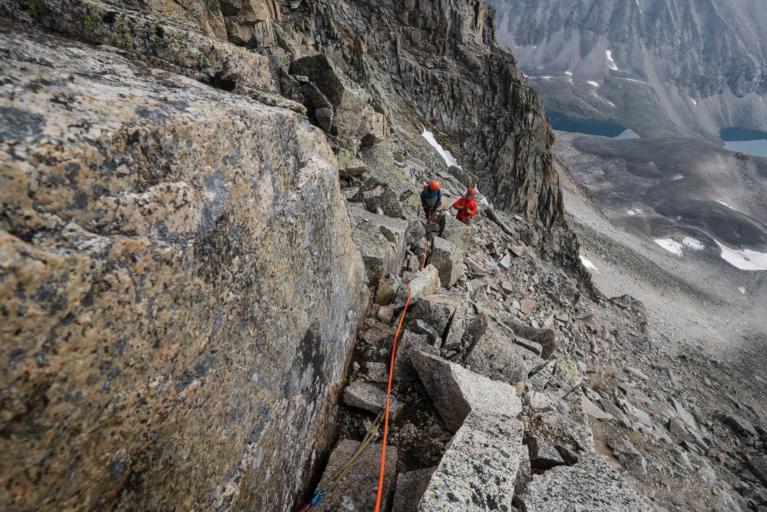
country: RU
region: Transbaikal Territory
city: Chara
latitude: 56.8657
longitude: 117.5815
